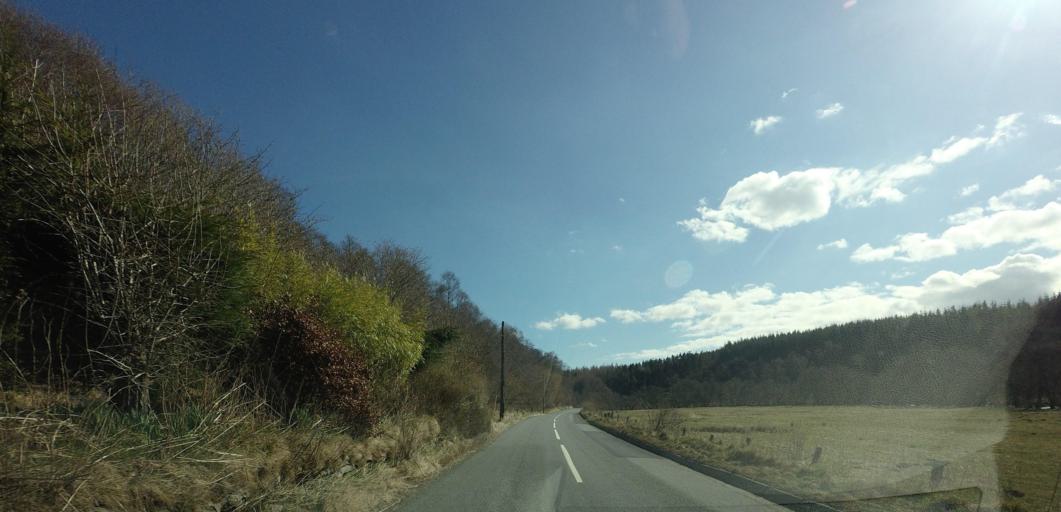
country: GB
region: Scotland
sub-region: Perth and Kinross
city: Methven
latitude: 56.5378
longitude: -3.6816
